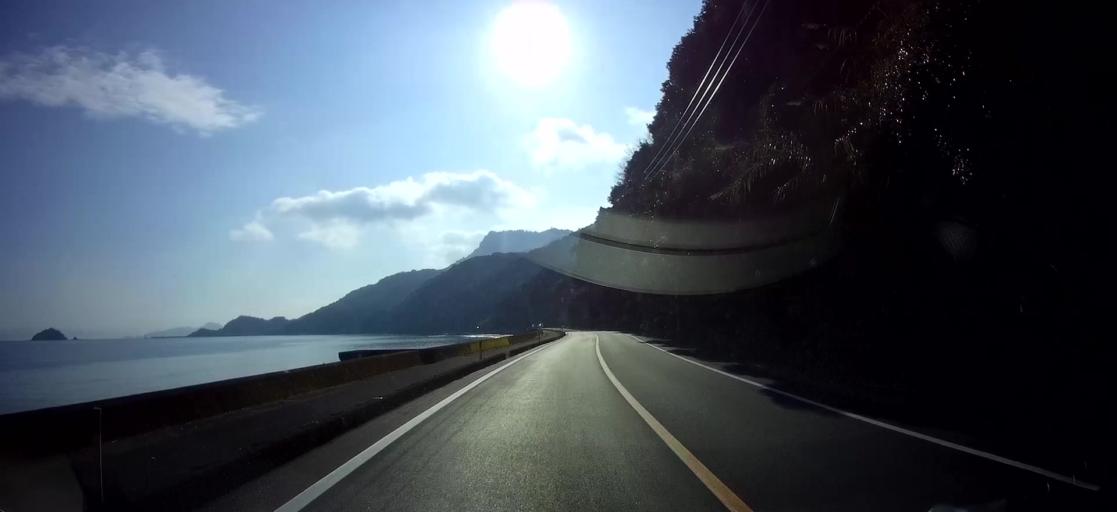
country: JP
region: Kumamoto
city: Yatsushiro
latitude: 32.4904
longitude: 130.4406
